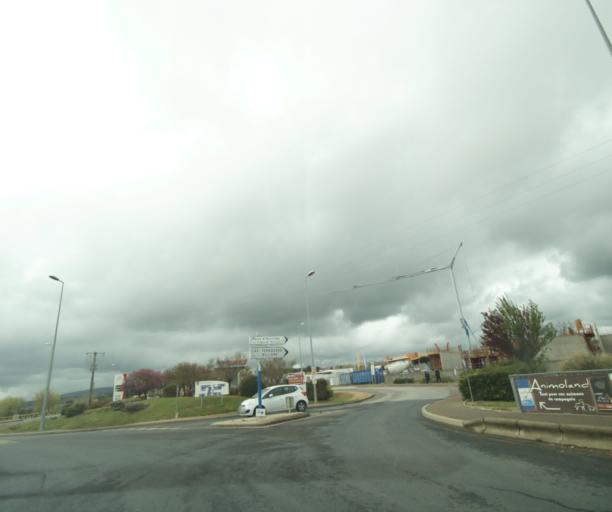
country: FR
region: Languedoc-Roussillon
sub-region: Departement de l'Herault
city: Cournonterral
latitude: 43.5504
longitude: 3.7162
